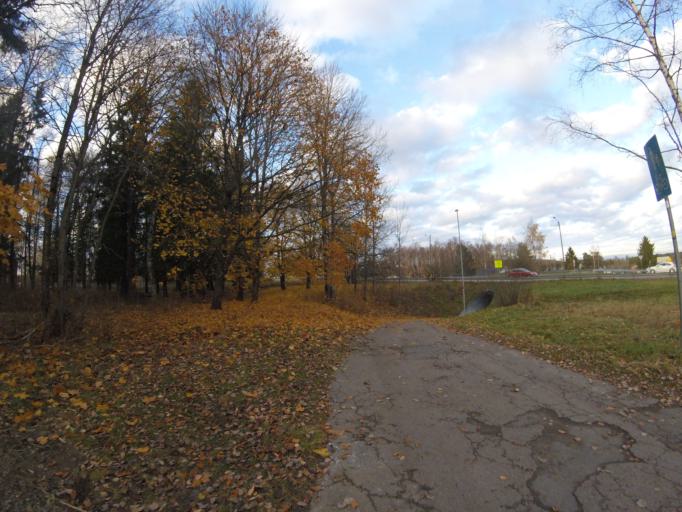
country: NO
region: Akershus
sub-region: Skedsmo
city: Lillestrom
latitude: 59.9967
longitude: 11.0434
